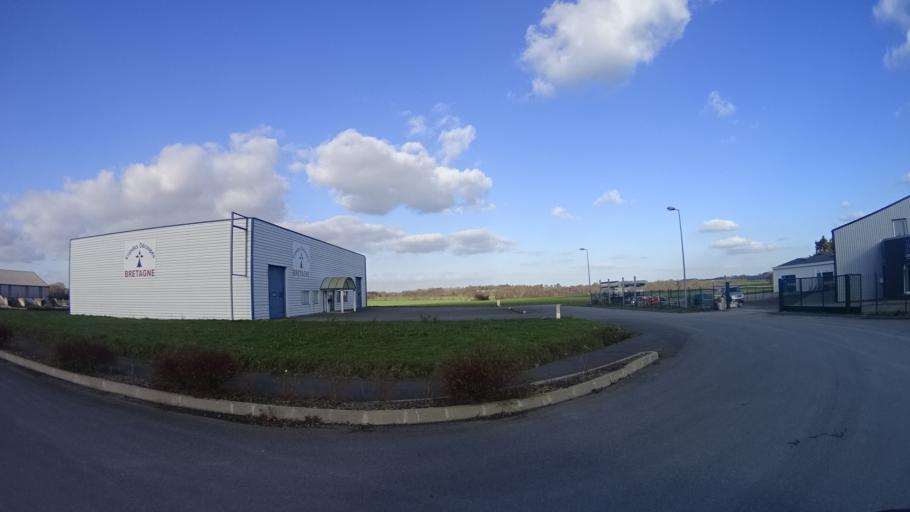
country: FR
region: Pays de la Loire
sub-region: Departement de la Loire-Atlantique
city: Guemene-Penfao
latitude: 47.6357
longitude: -1.8009
